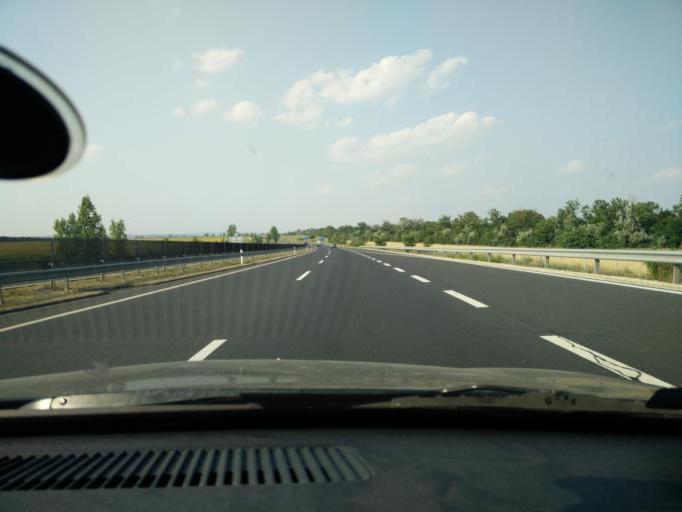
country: HU
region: Pest
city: Szazhalombatta
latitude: 47.3409
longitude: 18.8968
